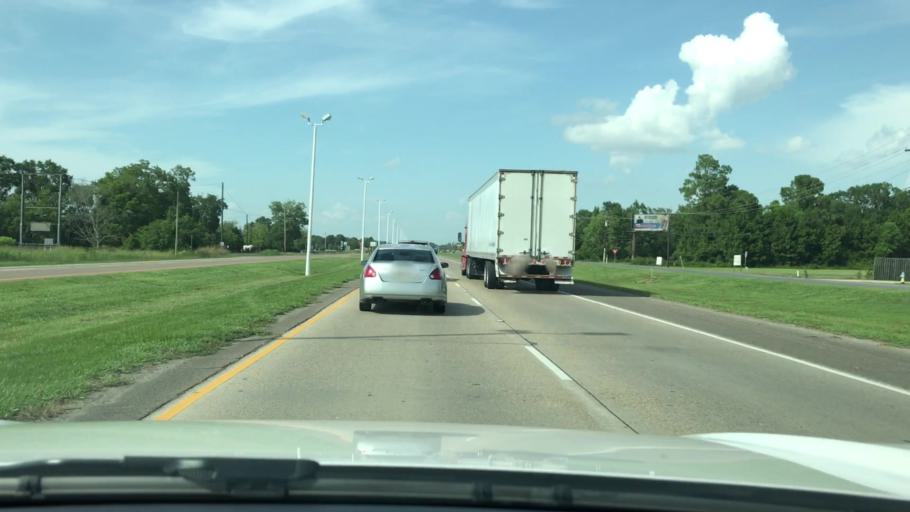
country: US
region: Louisiana
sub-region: West Baton Rouge Parish
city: Addis
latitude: 30.3676
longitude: -91.2589
